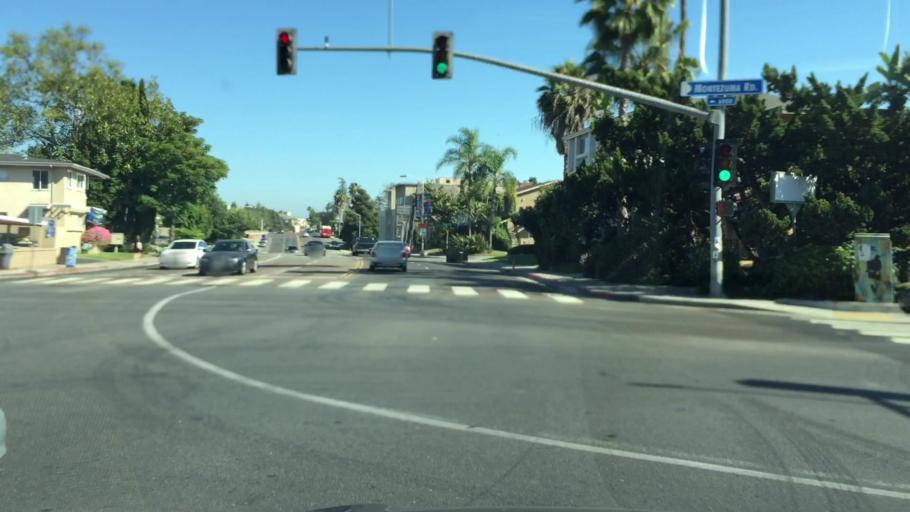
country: US
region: California
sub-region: San Diego County
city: La Mesa
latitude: 32.7708
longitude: -117.0700
